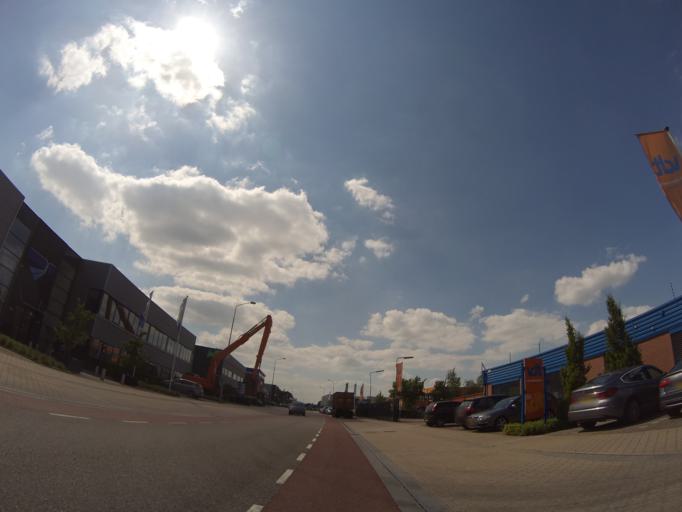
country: NL
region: Gelderland
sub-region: Gemeente Barneveld
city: Barneveld
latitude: 52.1645
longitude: 5.5811
